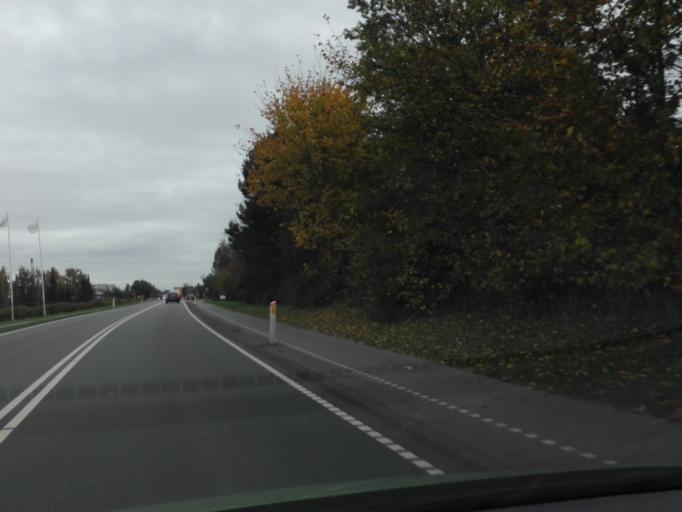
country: DK
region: Central Jutland
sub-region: Skanderborg Kommune
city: Horning
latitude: 56.0926
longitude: 10.0479
